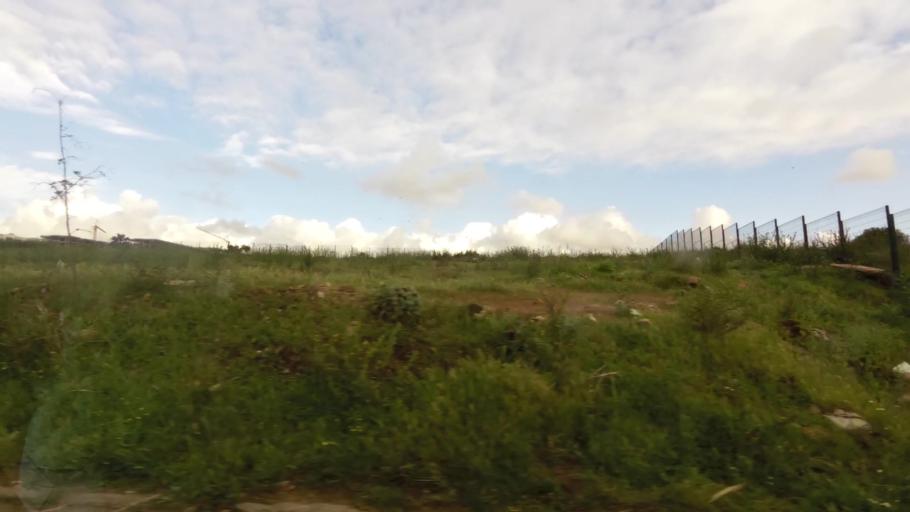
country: MA
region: Grand Casablanca
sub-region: Casablanca
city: Casablanca
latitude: 33.5802
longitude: -7.6868
